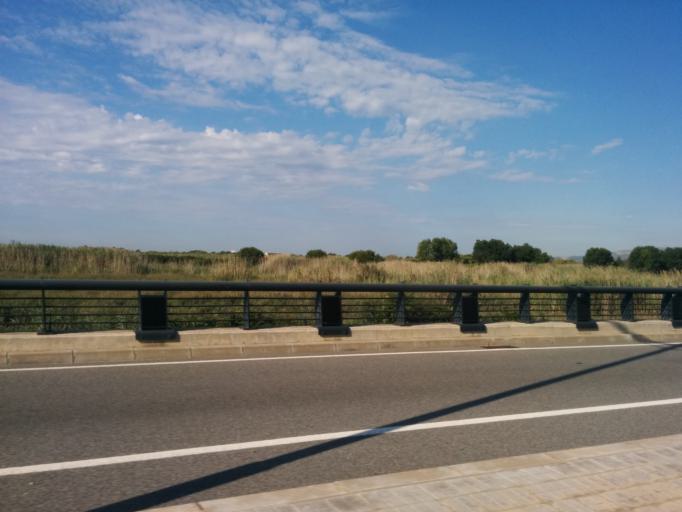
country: ES
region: Catalonia
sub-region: Provincia de Barcelona
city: El Prat de Llobregat
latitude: 41.2881
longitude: 2.0654
